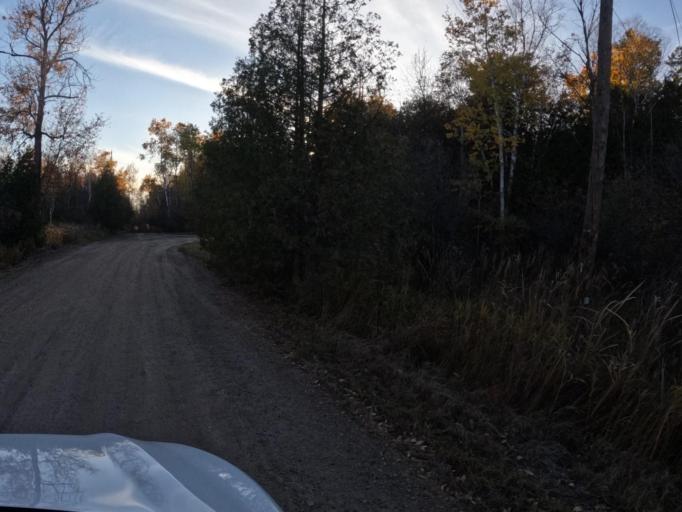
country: CA
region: Ontario
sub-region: Wellington County
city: Guelph
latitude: 43.4725
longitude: -80.1200
